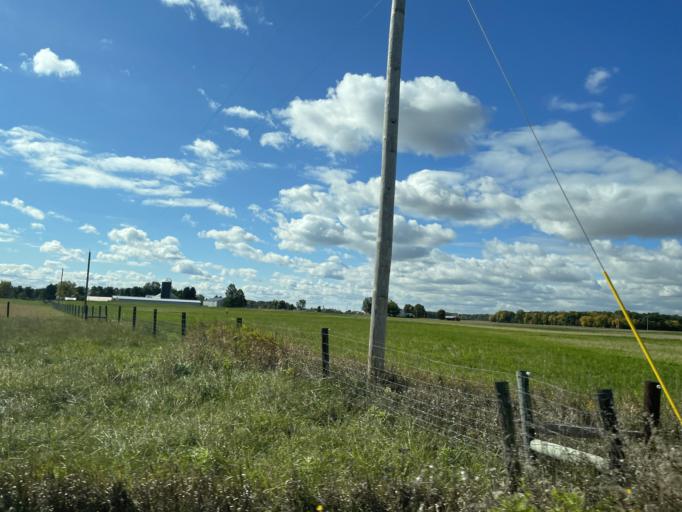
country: US
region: Indiana
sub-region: Whitley County
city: Churubusco
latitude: 41.1241
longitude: -85.2818
